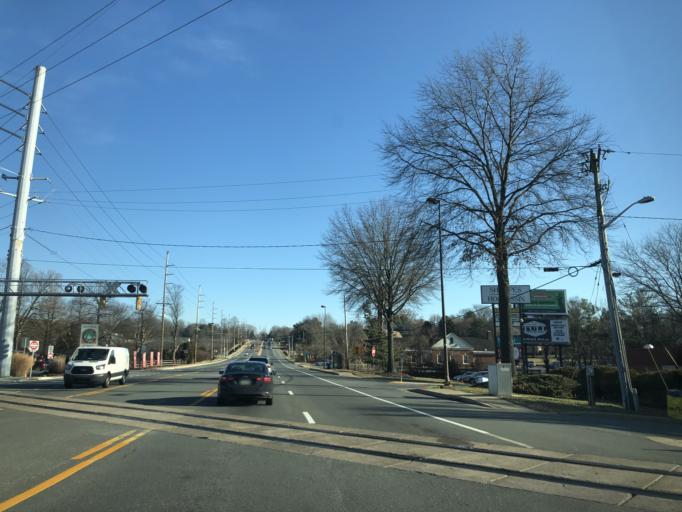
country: US
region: Delaware
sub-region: New Castle County
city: Hockessin
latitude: 39.7879
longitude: -75.6934
